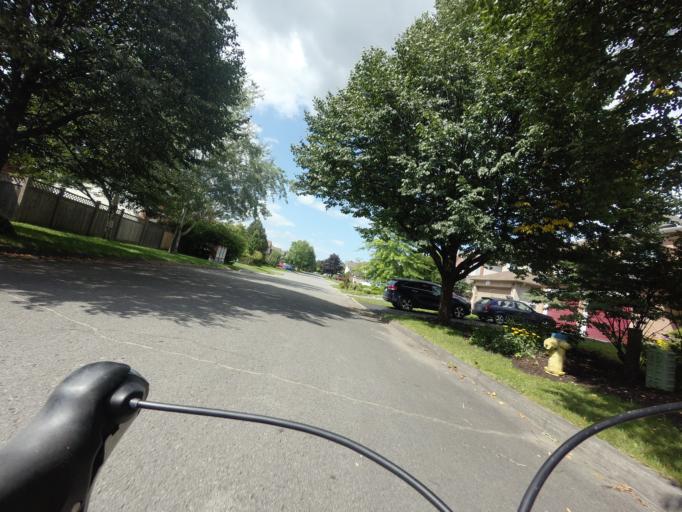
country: CA
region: Ontario
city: Bells Corners
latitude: 45.2768
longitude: -75.8491
